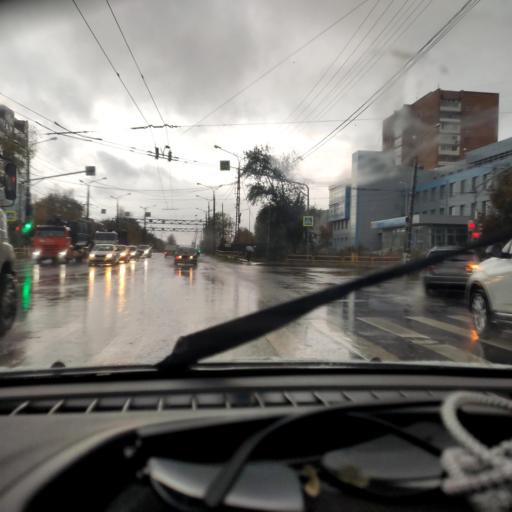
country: RU
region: Samara
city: Zhigulevsk
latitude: 53.4817
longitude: 49.4863
